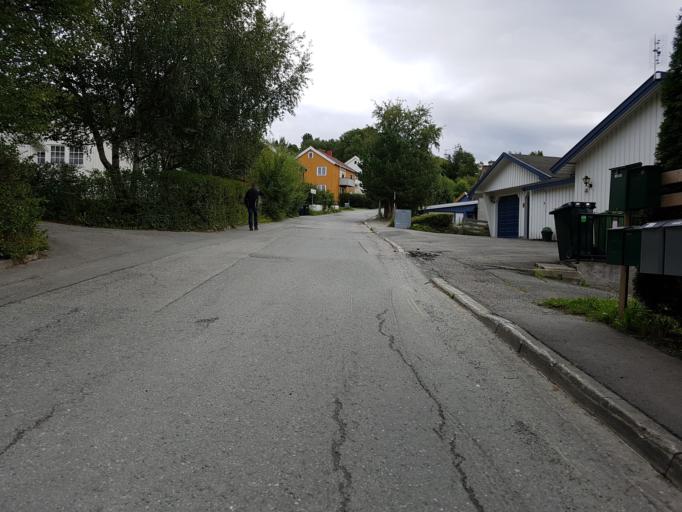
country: NO
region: Sor-Trondelag
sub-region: Trondheim
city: Trondheim
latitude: 63.3981
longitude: 10.4128
